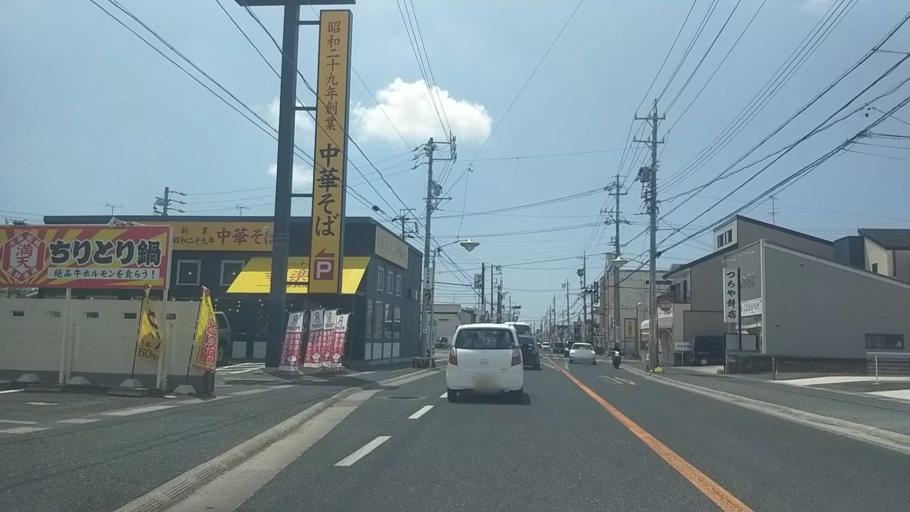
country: JP
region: Shizuoka
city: Hamamatsu
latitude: 34.7436
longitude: 137.7240
